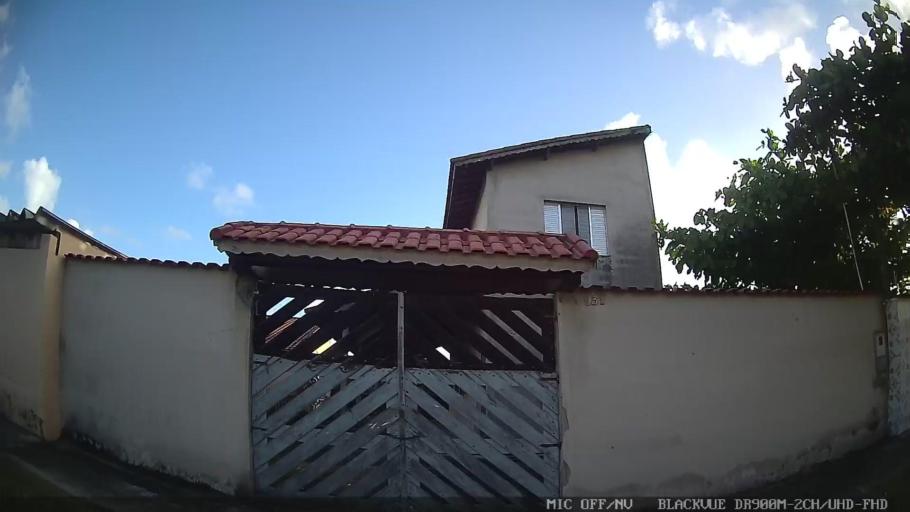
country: BR
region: Sao Paulo
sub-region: Itanhaem
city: Itanhaem
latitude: -24.1395
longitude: -46.7197
